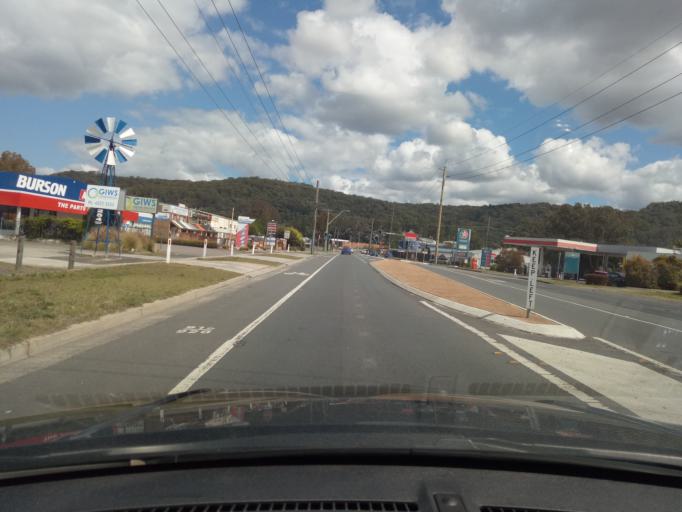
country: AU
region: New South Wales
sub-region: Gosford Shire
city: Gosford
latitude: -33.4169
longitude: 151.3260
